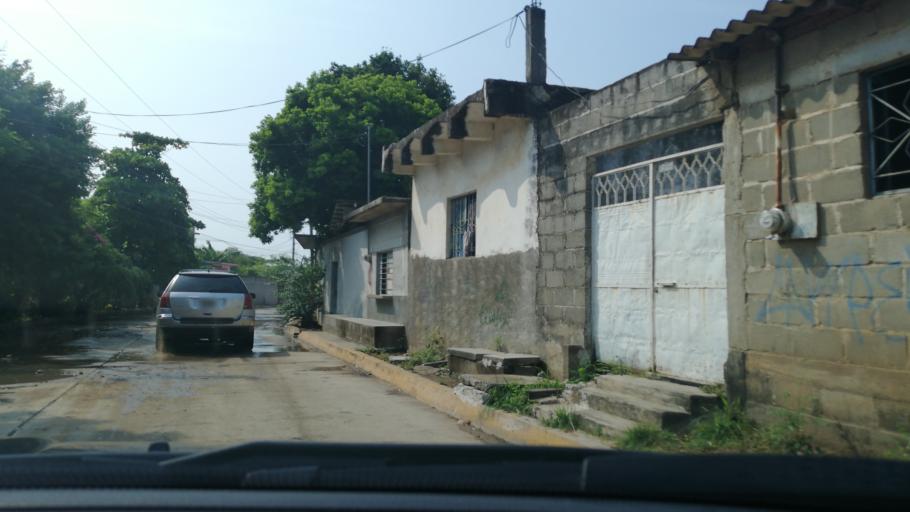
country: MX
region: Oaxaca
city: San Blas Atempa
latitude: 16.3392
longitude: -95.2209
